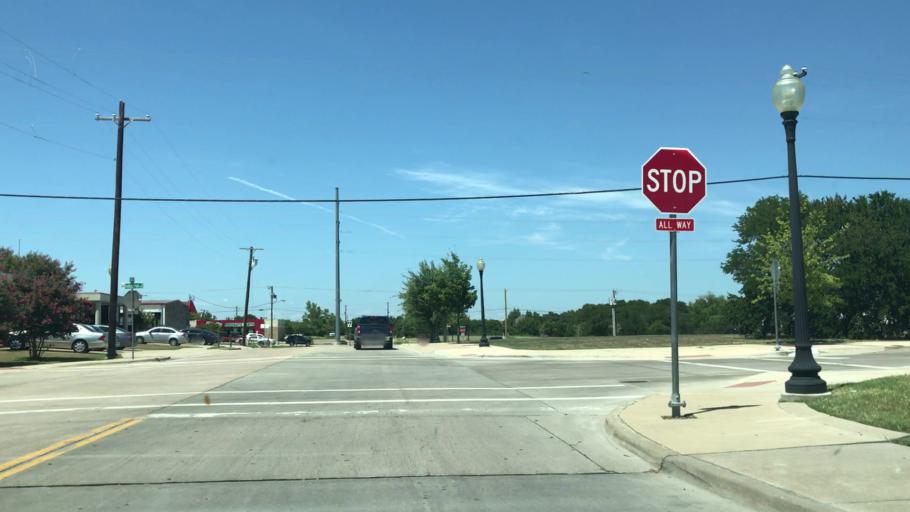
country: US
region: Texas
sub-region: Dallas County
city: Rowlett
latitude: 32.9061
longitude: -96.5636
